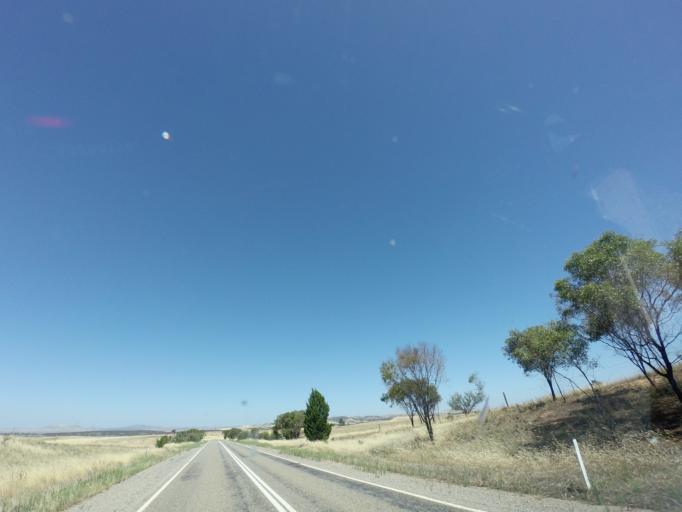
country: AU
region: South Australia
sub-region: Peterborough
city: Peterborough
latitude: -32.7463
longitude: 138.5613
